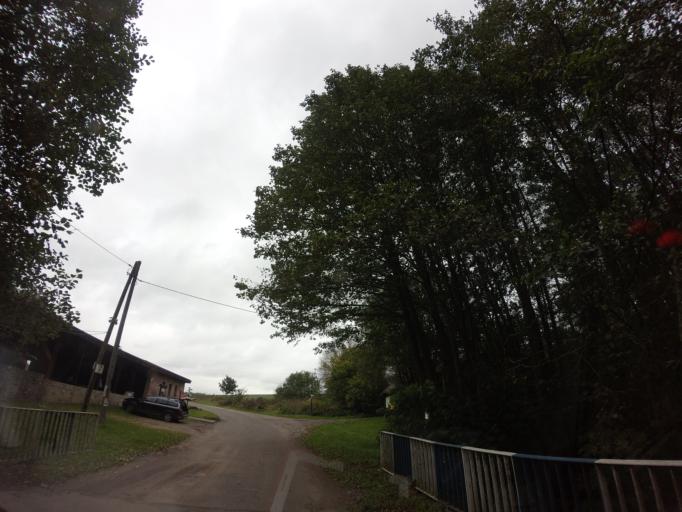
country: PL
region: West Pomeranian Voivodeship
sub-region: Powiat choszczenski
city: Drawno
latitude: 53.2029
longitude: 15.7622
